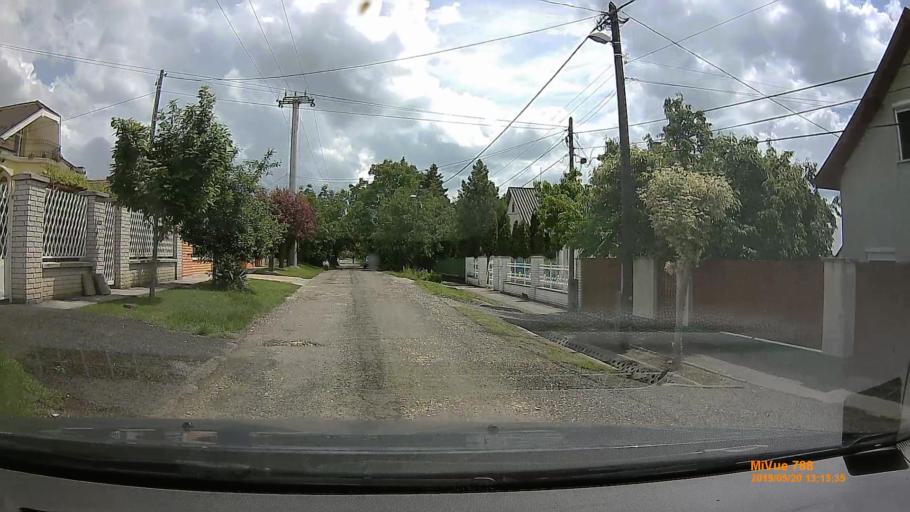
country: HU
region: Pest
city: Ecser
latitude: 47.4649
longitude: 19.3004
